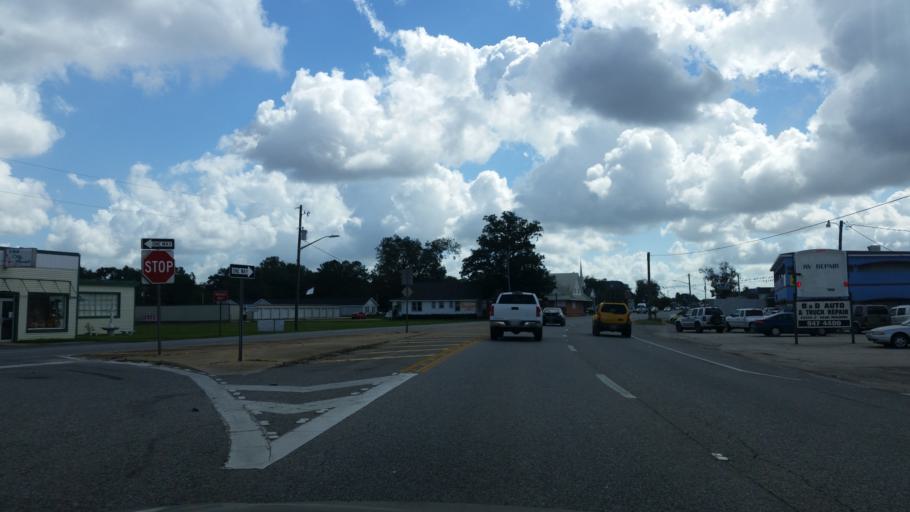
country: US
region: Alabama
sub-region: Baldwin County
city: Robertsdale
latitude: 30.5511
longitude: -87.7086
